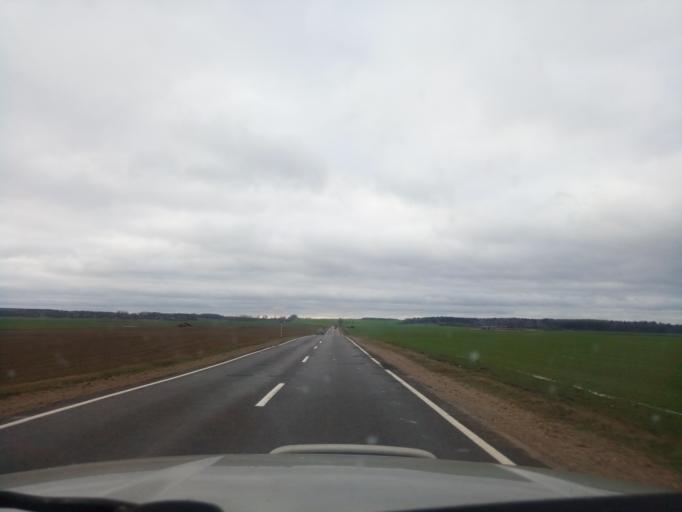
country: BY
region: Minsk
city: Kapyl'
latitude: 53.1956
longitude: 27.1979
